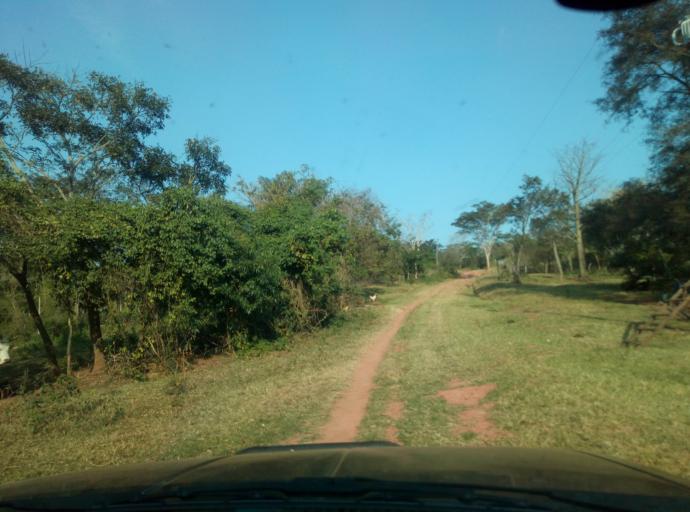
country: PY
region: Caaguazu
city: San Joaquin
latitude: -25.1559
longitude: -56.1204
